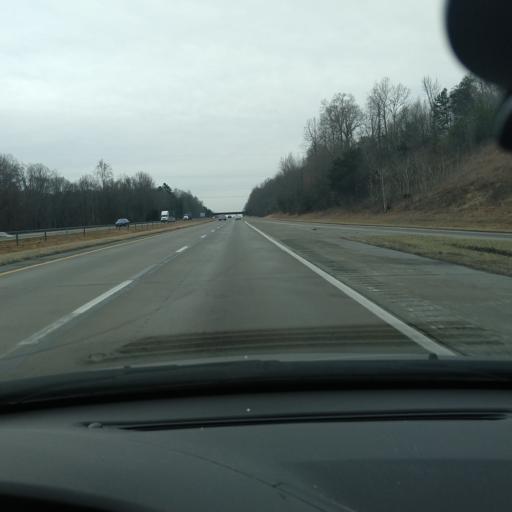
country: US
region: North Carolina
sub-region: Davidson County
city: Midway
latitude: 36.0129
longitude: -80.2357
